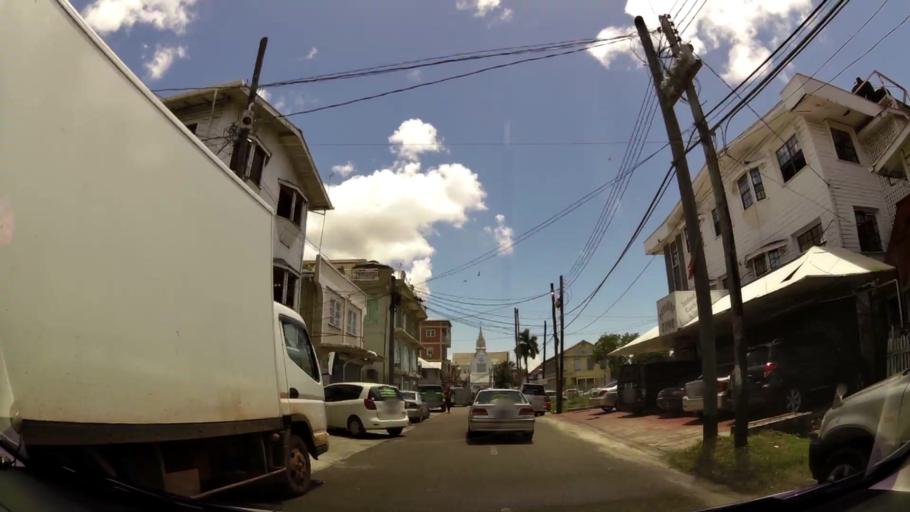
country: GY
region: Demerara-Mahaica
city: Georgetown
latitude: 6.8121
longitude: -58.1615
